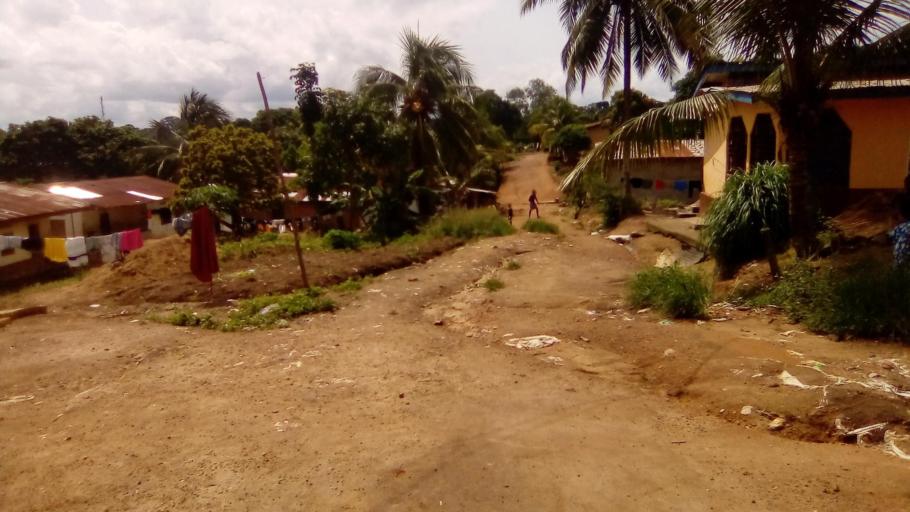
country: SL
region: Southern Province
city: Bo
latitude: 7.9790
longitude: -11.7443
